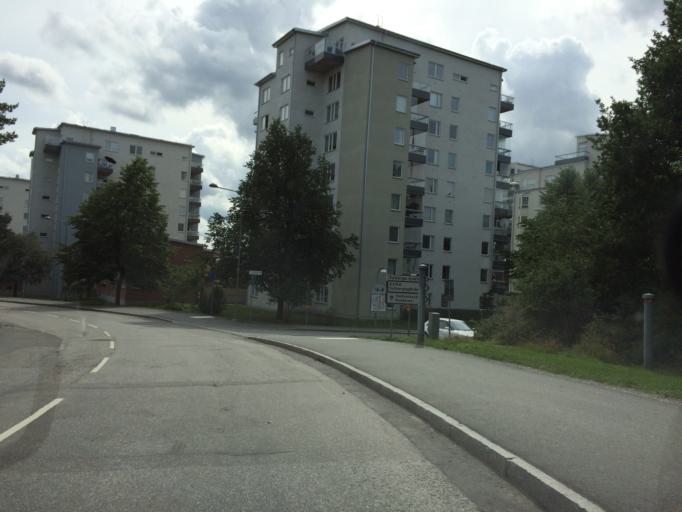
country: SE
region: Stockholm
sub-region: Stockholms Kommun
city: Arsta
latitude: 59.2835
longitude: 18.0116
